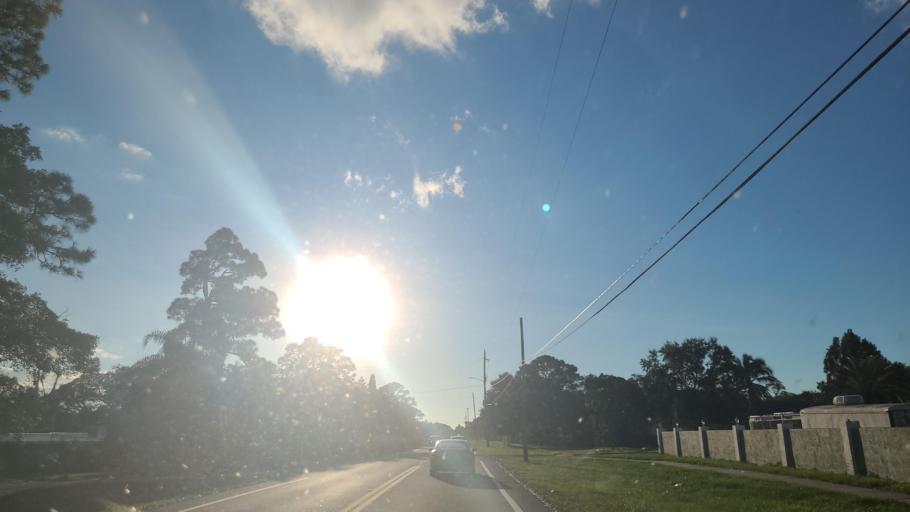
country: US
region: Florida
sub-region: Indian River County
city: Vero Beach South
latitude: 27.6090
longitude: -80.3922
